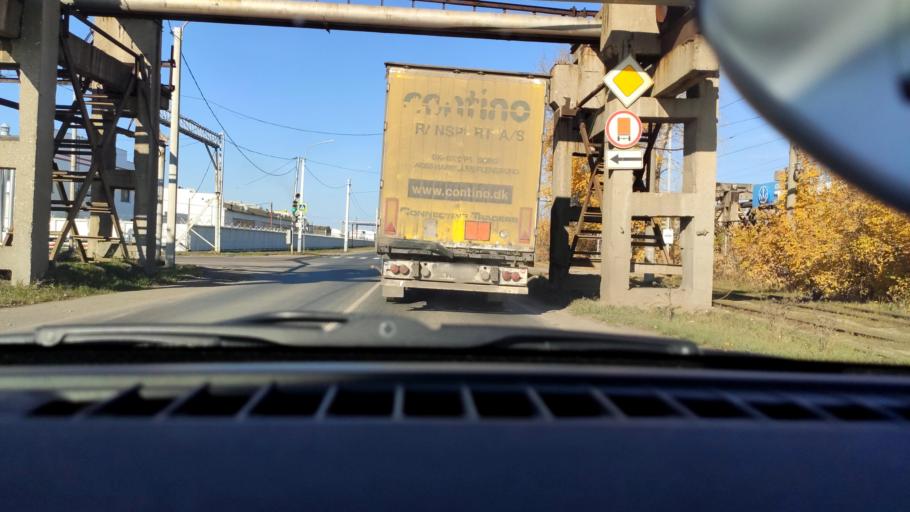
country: RU
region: Perm
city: Gamovo
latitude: 57.9139
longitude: 56.1556
